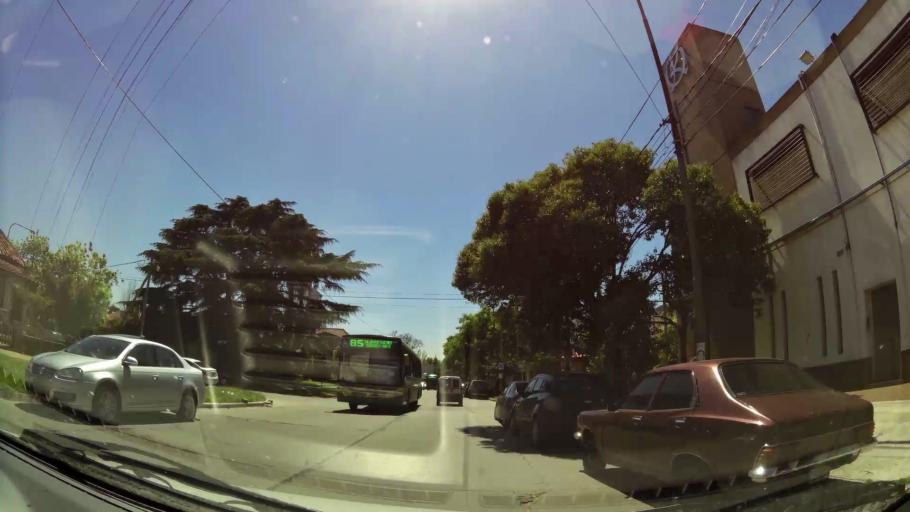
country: AR
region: Buenos Aires
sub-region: Partido de Quilmes
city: Quilmes
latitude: -34.7173
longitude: -58.2767
